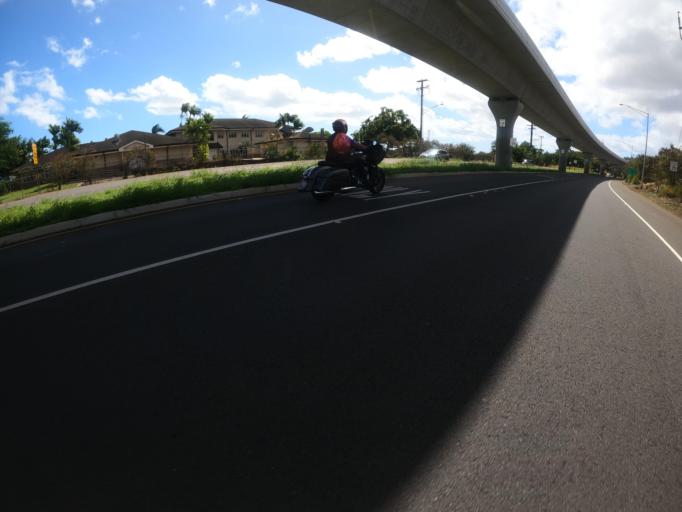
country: US
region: Hawaii
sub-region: Honolulu County
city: Royal Kunia
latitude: 21.3751
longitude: -158.0291
